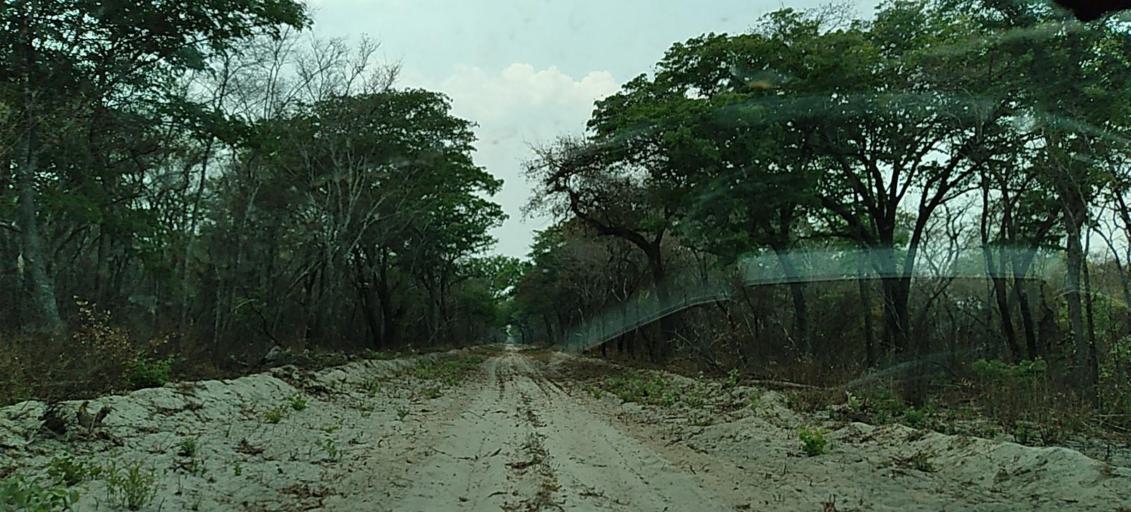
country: ZM
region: Western
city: Lukulu
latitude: -14.0160
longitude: 23.5798
